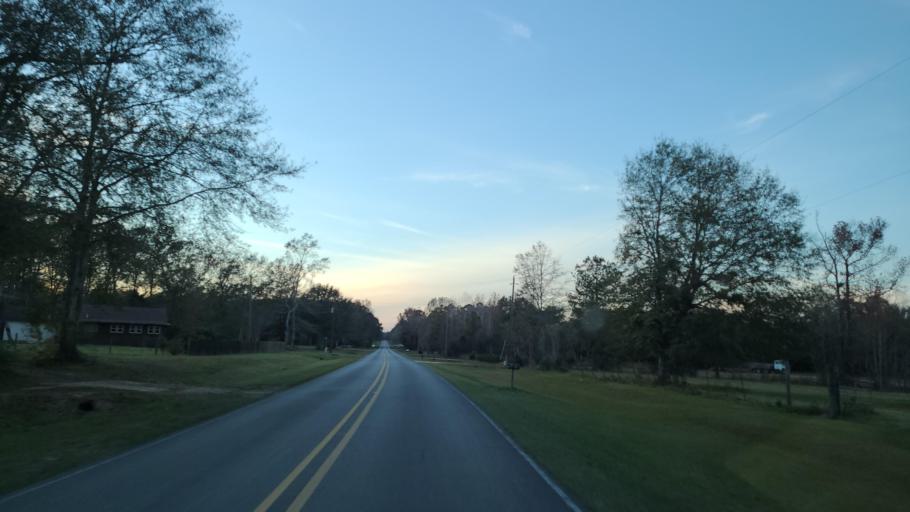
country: US
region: Mississippi
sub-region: Perry County
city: New Augusta
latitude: 31.0696
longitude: -89.1958
